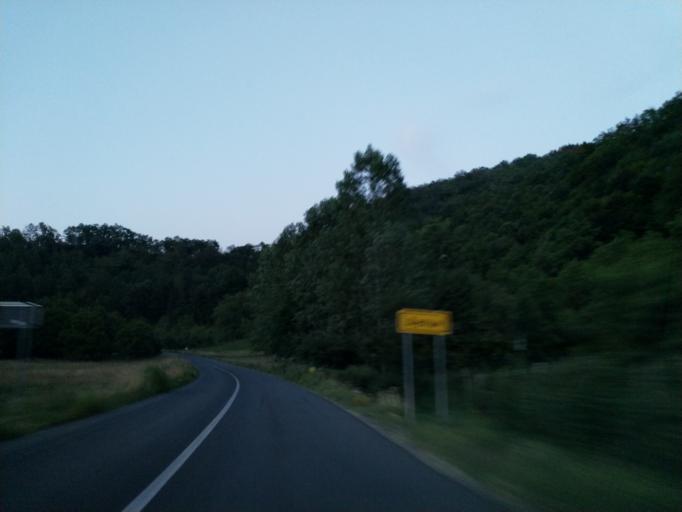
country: RS
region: Central Serbia
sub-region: Rasinski Okrug
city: Aleksandrovac
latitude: 43.3420
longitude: 21.1135
